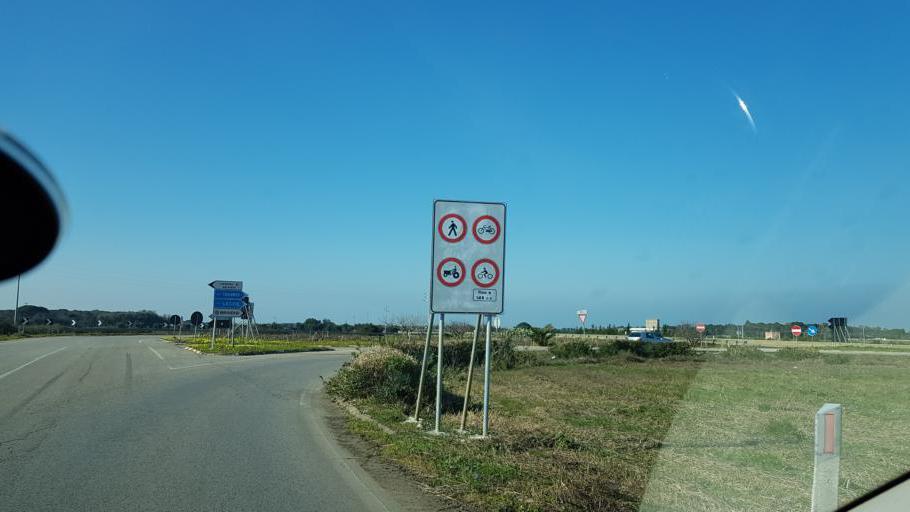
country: IT
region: Apulia
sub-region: Provincia di Brindisi
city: Brindisi
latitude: 40.6557
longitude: 17.8963
